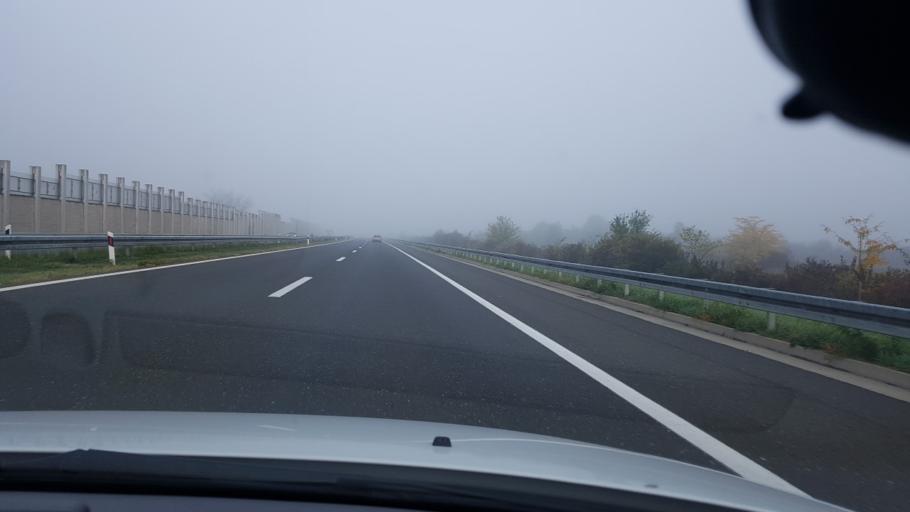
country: HR
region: Zagrebacka
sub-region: Grad Samobor
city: Samobor
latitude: 45.8126
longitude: 15.7642
